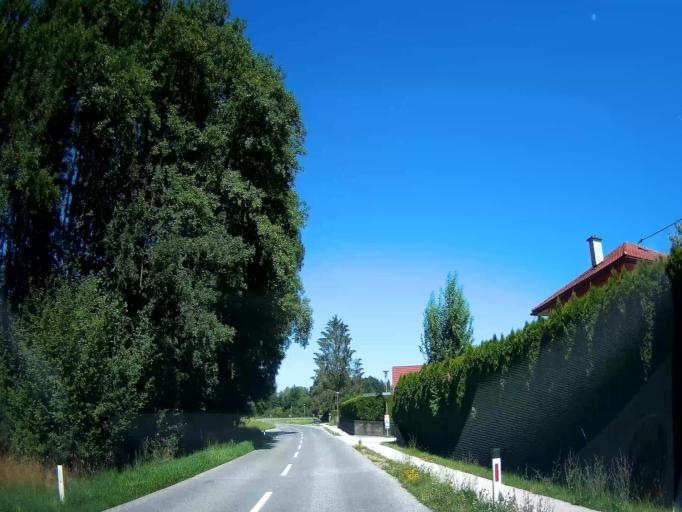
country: AT
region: Carinthia
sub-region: Politischer Bezirk Klagenfurt Land
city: Ebenthal
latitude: 46.6057
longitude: 14.4035
